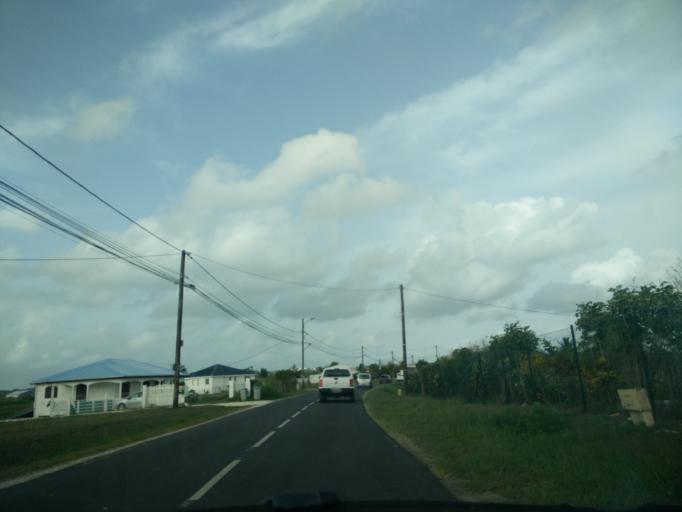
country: GP
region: Guadeloupe
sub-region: Guadeloupe
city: Le Moule
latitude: 16.2851
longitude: -61.3706
